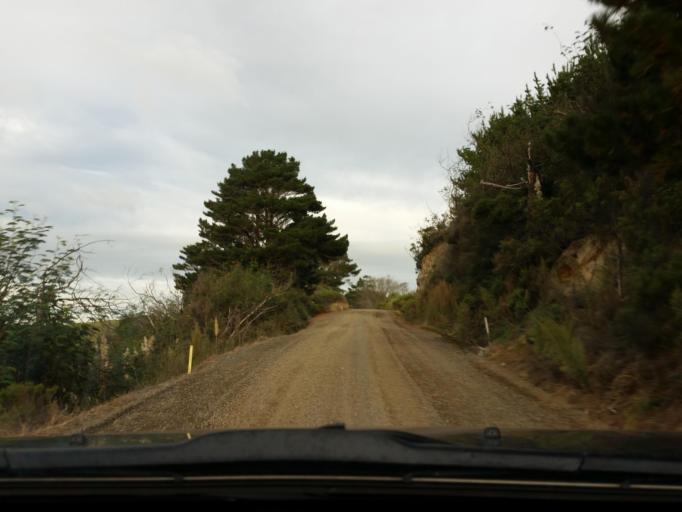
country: NZ
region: Northland
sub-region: Kaipara District
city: Dargaville
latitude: -35.8844
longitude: 173.7087
